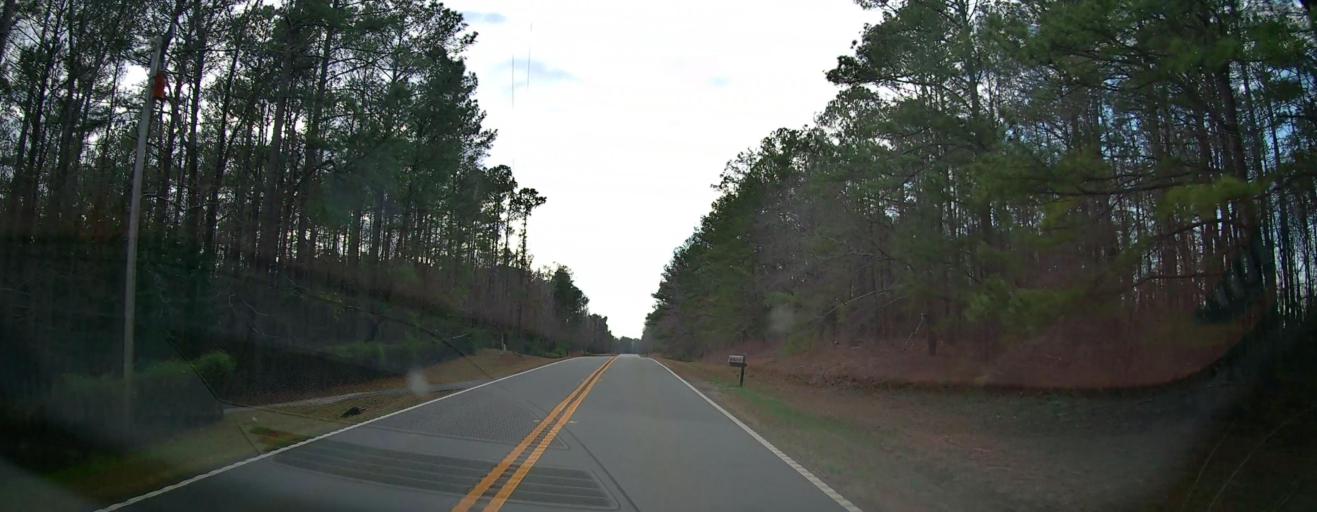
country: US
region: Georgia
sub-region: Harris County
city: Hamilton
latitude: 32.7018
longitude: -84.8449
